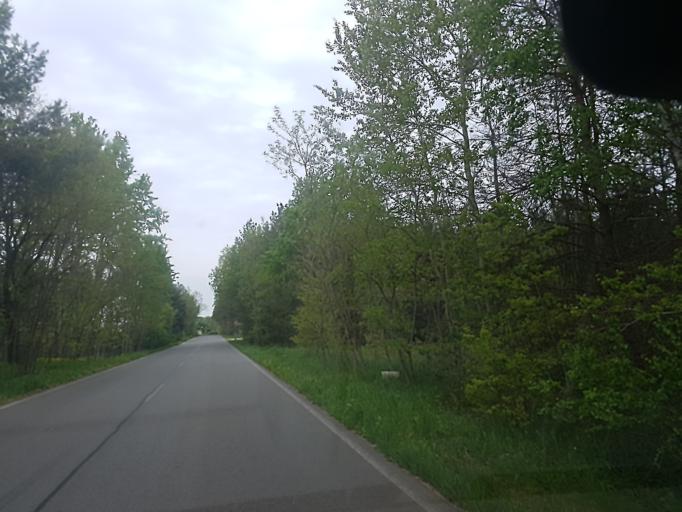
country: DE
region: Brandenburg
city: Finsterwalde
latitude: 51.6091
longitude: 13.7616
